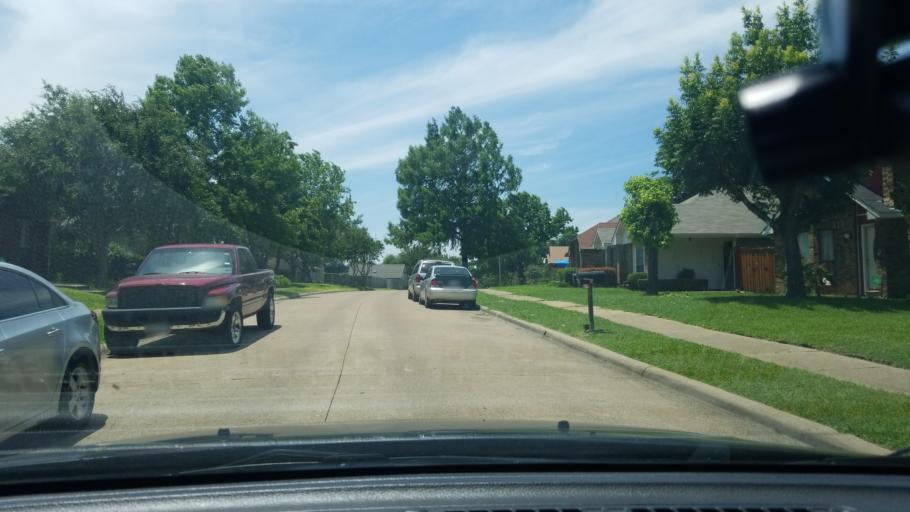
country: US
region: Texas
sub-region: Dallas County
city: Mesquite
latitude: 32.7837
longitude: -96.5968
